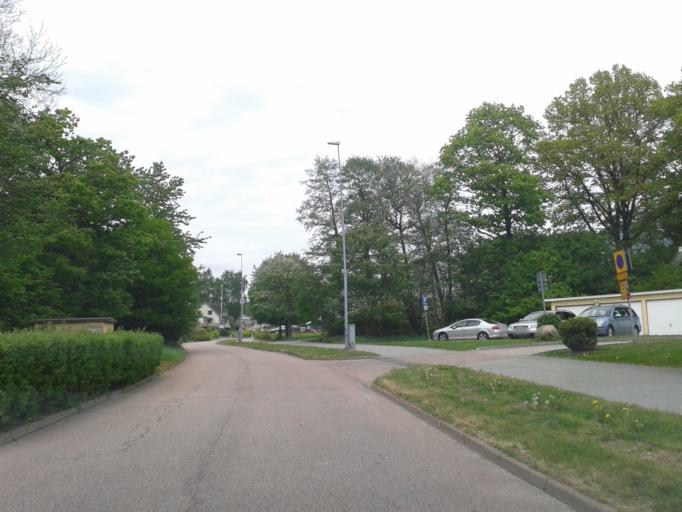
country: SE
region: Vaestra Goetaland
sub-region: Kungalvs Kommun
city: Kungalv
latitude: 57.8843
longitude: 11.9527
